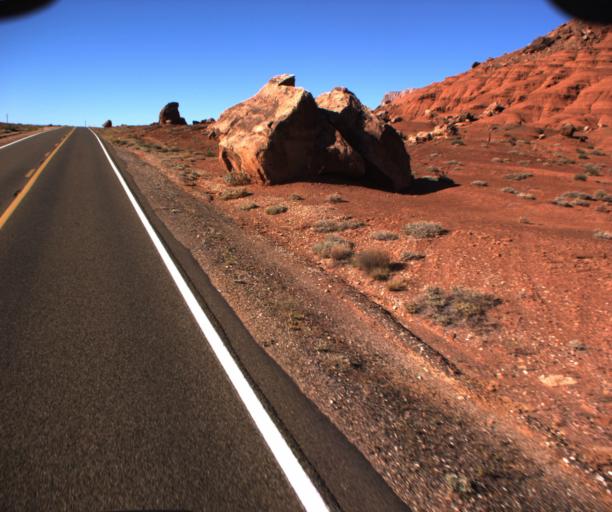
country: US
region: Arizona
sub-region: Coconino County
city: Page
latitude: 36.7570
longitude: -111.7152
